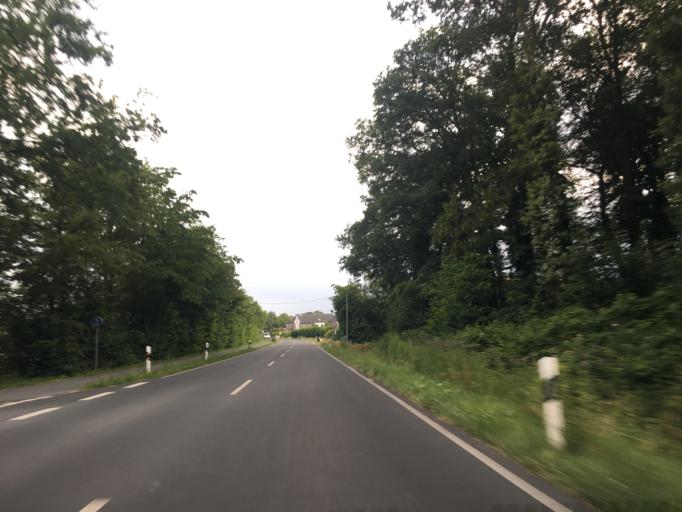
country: DE
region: North Rhine-Westphalia
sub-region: Regierungsbezirk Munster
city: Senden
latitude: 51.9286
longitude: 7.5280
